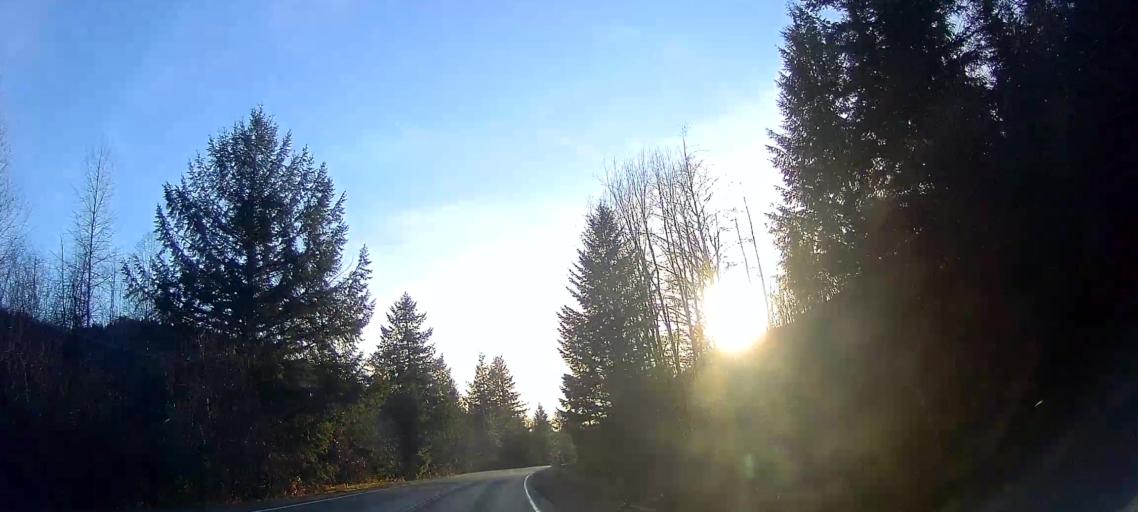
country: US
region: Washington
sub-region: Snohomish County
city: Darrington
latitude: 48.5950
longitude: -121.7701
